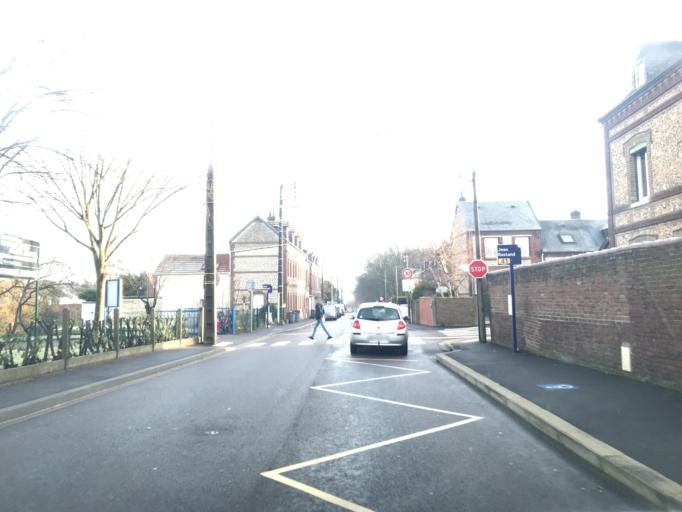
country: FR
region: Haute-Normandie
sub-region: Departement de la Seine-Maritime
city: Sotteville-les-Rouen
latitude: 49.4116
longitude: 1.0804
